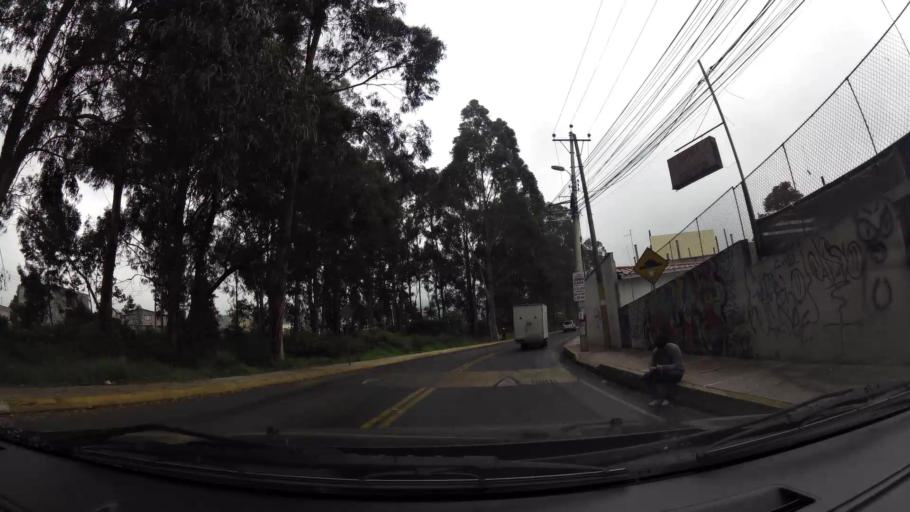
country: EC
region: Pichincha
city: Quito
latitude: -0.2668
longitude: -78.4723
